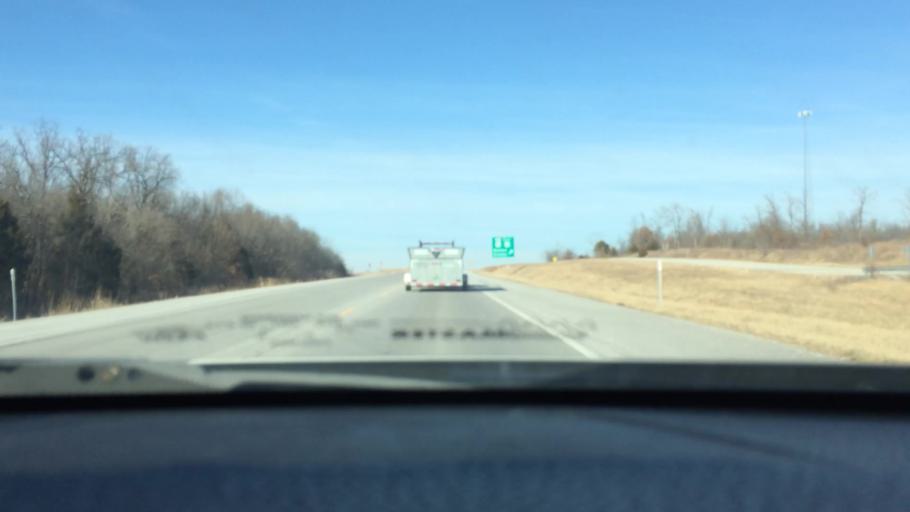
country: US
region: Missouri
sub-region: Newton County
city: Neosho
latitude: 36.8987
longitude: -94.3169
